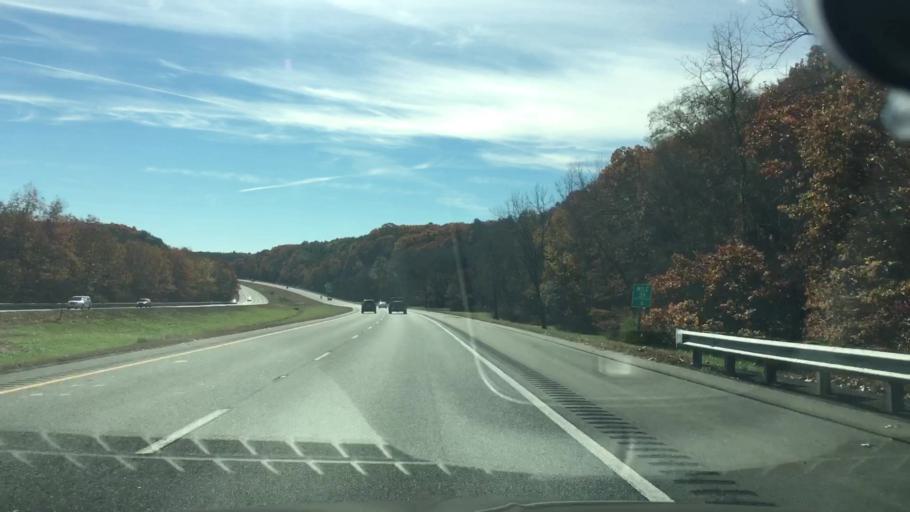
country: US
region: Massachusetts
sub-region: Franklin County
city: Greenfield
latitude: 42.5368
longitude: -72.6279
